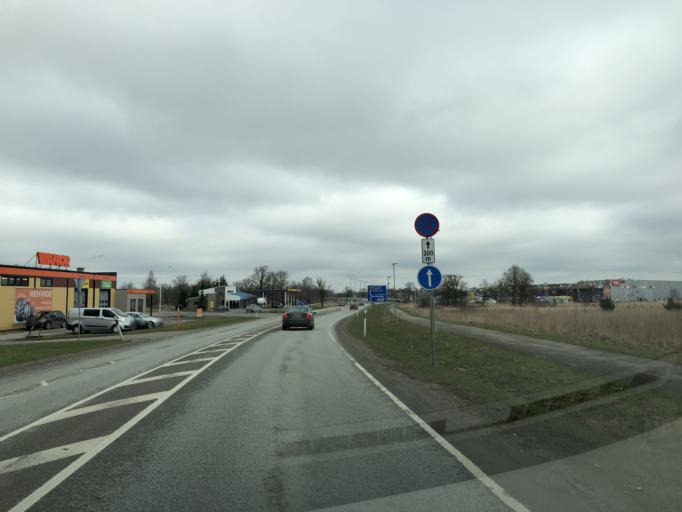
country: EE
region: Laeaene-Virumaa
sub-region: Rakvere linn
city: Rakvere
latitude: 59.3606
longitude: 26.3346
